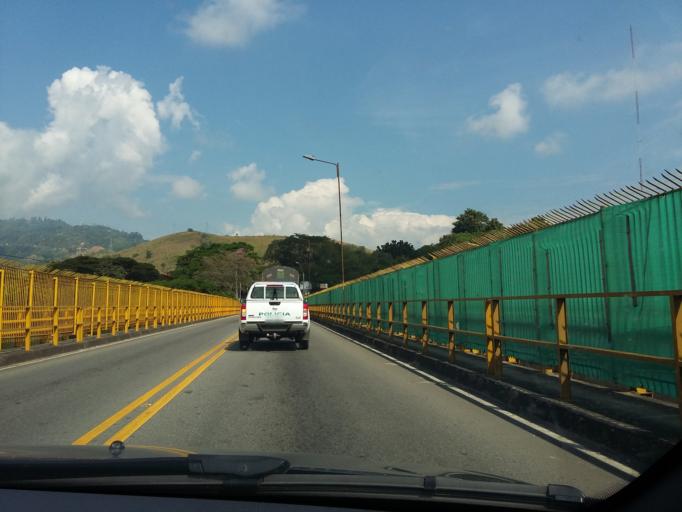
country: CO
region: Tolima
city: Ibague
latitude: 4.4055
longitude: -75.1817
